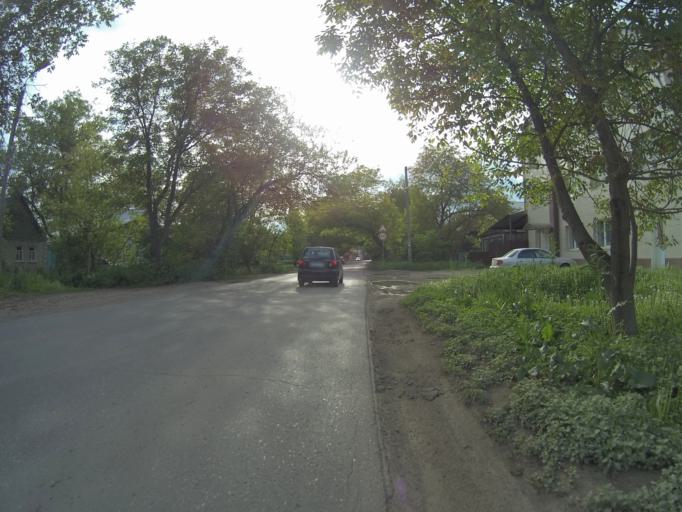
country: RU
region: Stavropol'skiy
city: Svobody
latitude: 44.0401
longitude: 43.0127
